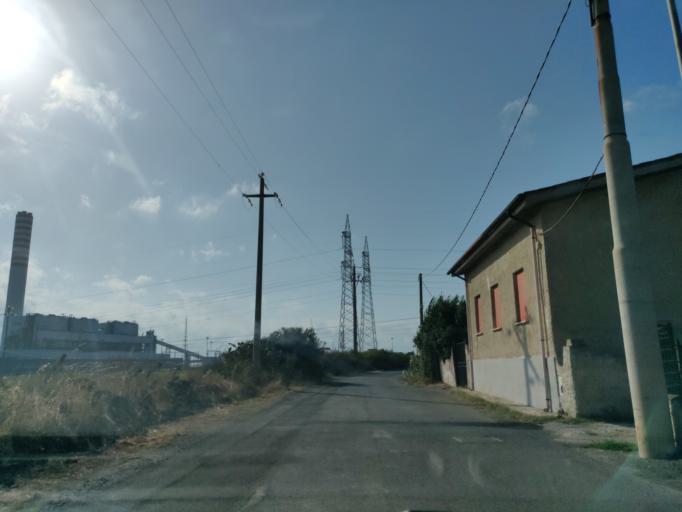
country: IT
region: Latium
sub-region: Citta metropolitana di Roma Capitale
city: Aurelia
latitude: 42.1279
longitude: 11.7685
